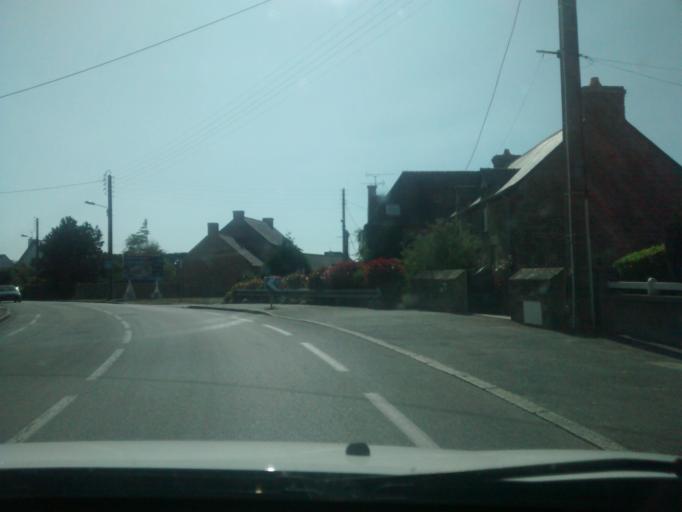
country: FR
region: Brittany
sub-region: Departement d'Ille-et-Vilaine
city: Saint-Malo
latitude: 48.6802
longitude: -1.9770
